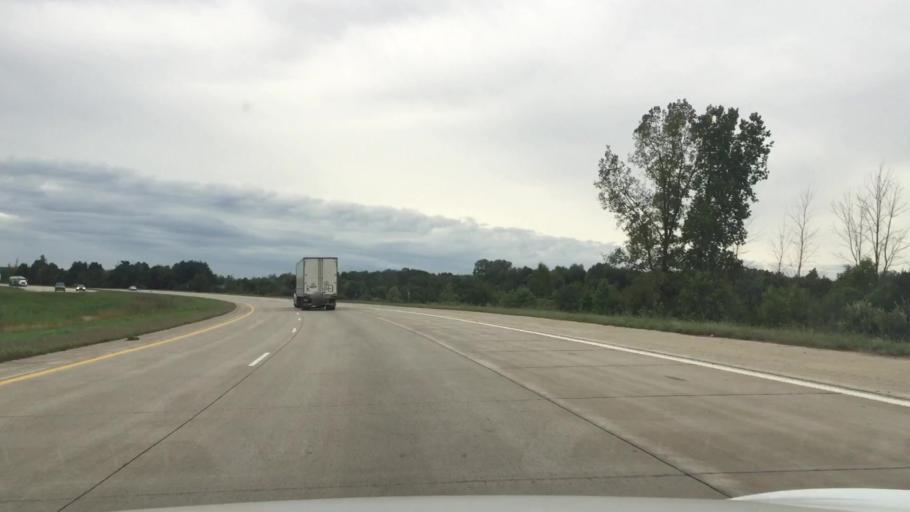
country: US
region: Michigan
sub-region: Saint Clair County
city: Marysville
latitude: 42.9485
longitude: -82.5072
